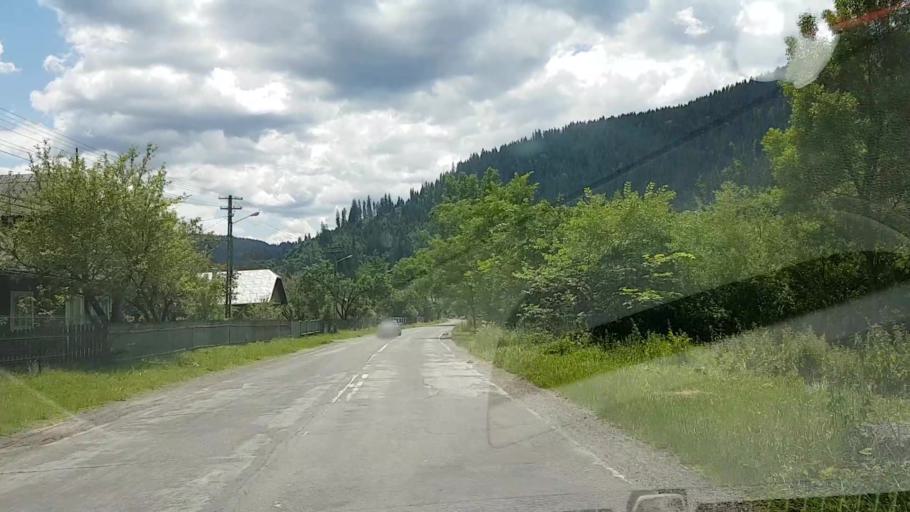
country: RO
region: Suceava
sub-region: Comuna Brosteni
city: Brosteni
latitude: 47.2468
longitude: 25.6916
